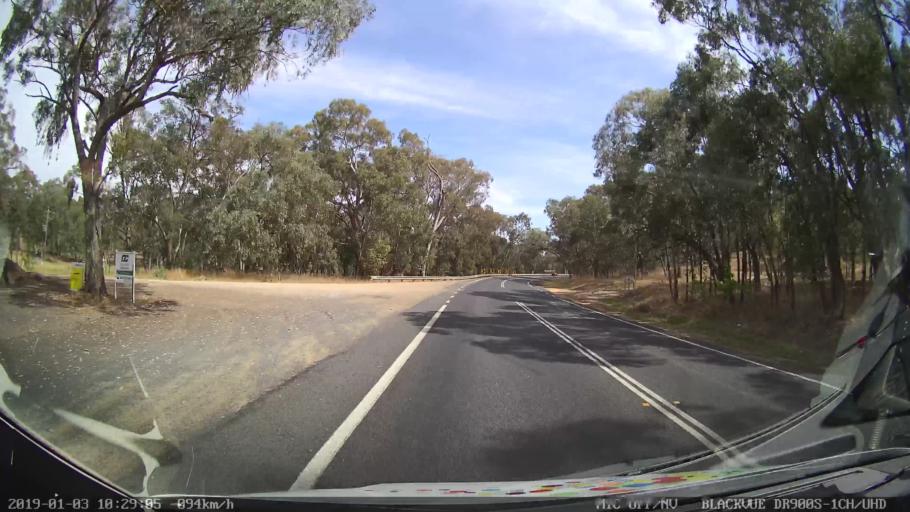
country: AU
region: New South Wales
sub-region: Young
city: Young
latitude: -34.3786
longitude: 148.2596
